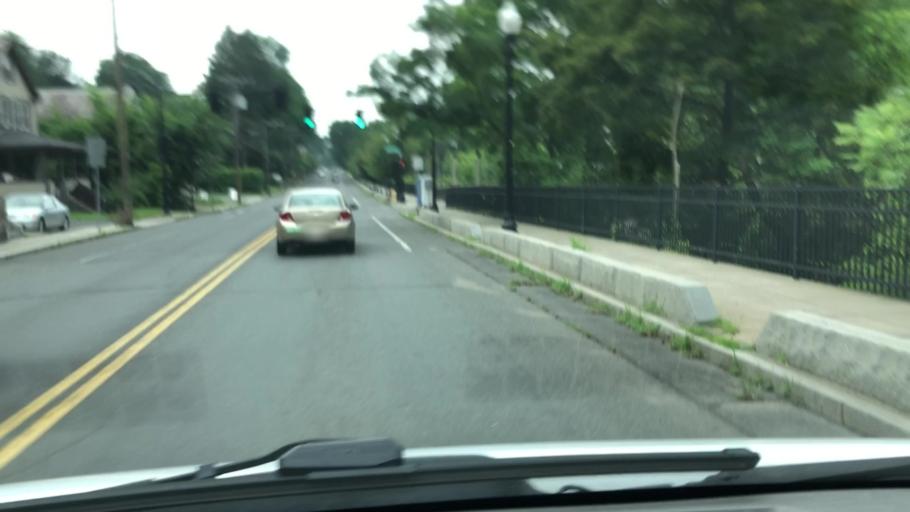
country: US
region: Massachusetts
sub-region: Franklin County
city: Greenfield
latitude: 42.5809
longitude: -72.5993
